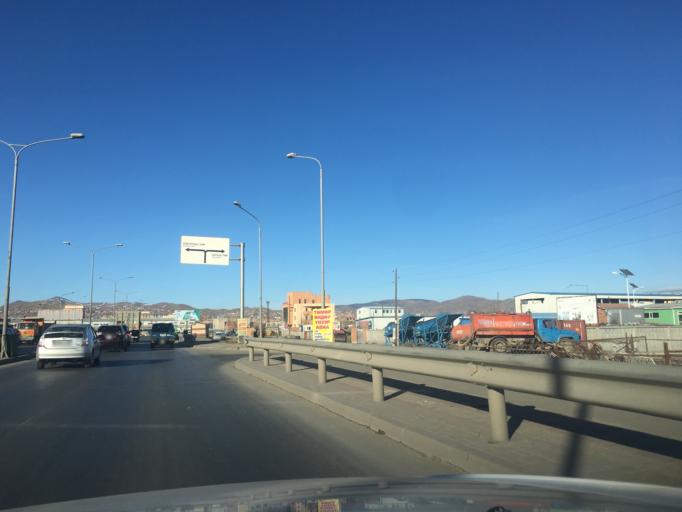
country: MN
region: Ulaanbaatar
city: Ulaanbaatar
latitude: 47.9045
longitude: 106.7861
